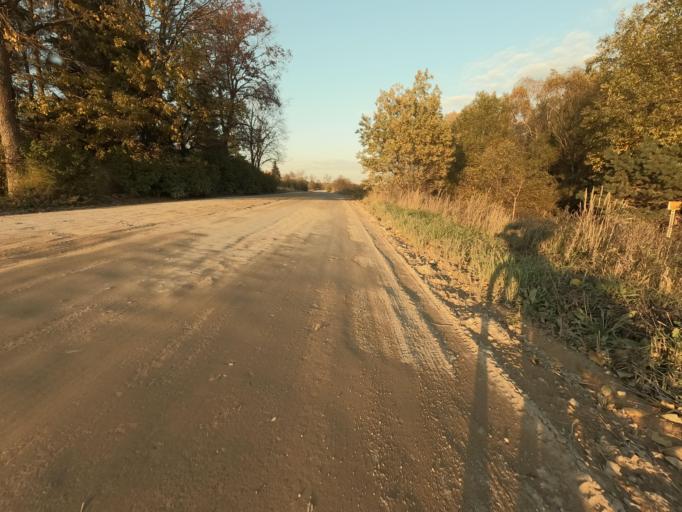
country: RU
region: Leningrad
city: Lyuban'
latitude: 59.0229
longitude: 31.0983
